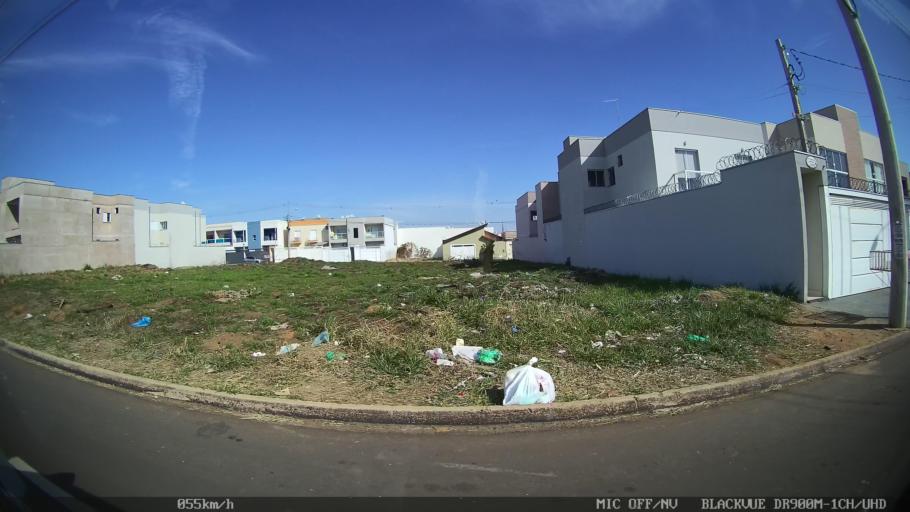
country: BR
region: Sao Paulo
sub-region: Franca
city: Franca
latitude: -20.5067
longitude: -47.4294
